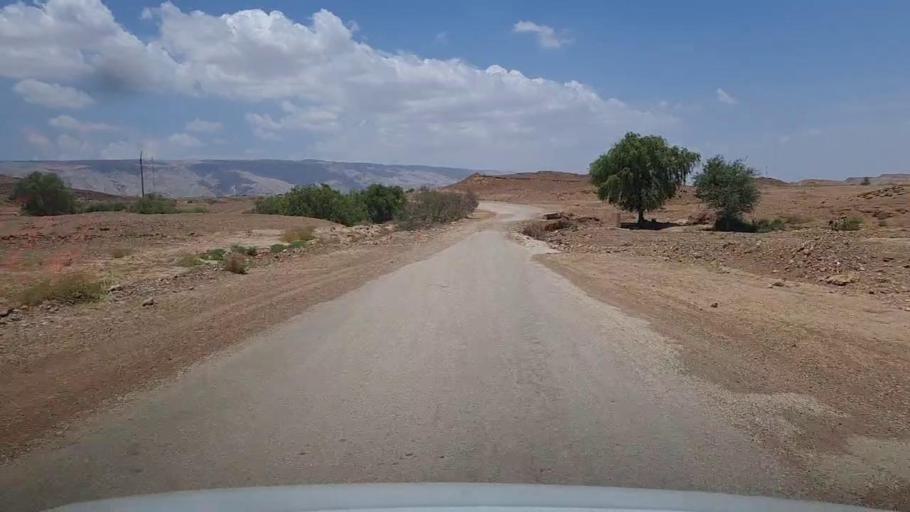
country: PK
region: Sindh
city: Bhan
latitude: 26.3180
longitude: 67.5604
